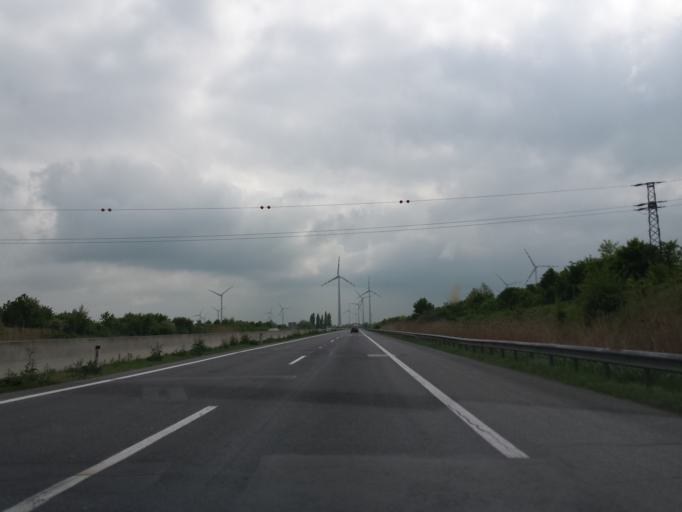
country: AT
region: Burgenland
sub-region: Politischer Bezirk Neusiedl am See
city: Zurndorf
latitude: 47.9311
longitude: 16.9993
